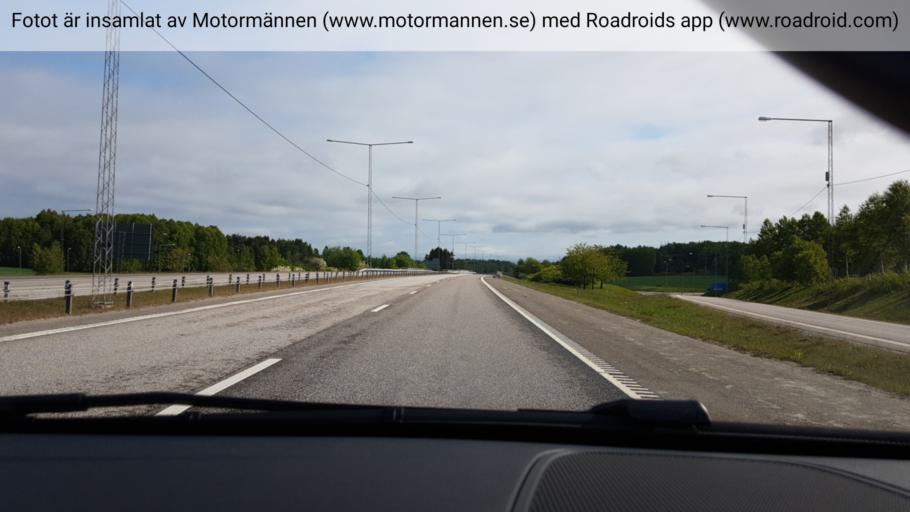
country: SE
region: Stockholm
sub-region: Haninge Kommun
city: Jordbro
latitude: 59.1199
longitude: 18.1307
